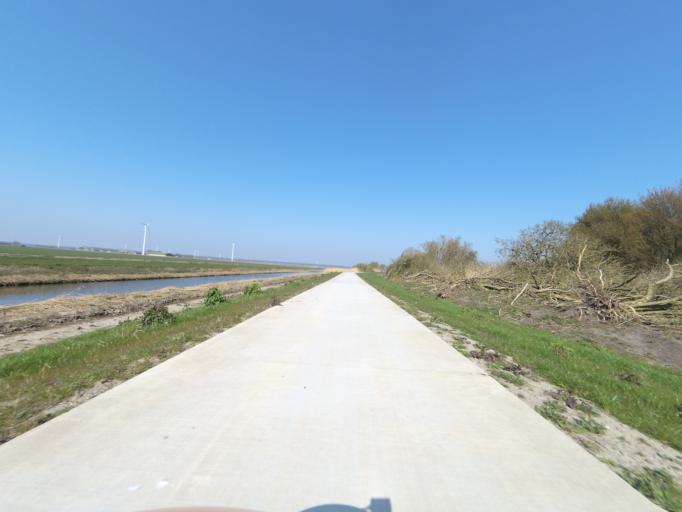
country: NL
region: Utrecht
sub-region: Gemeente Bunschoten
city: Spakenburg
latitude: 52.3498
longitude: 5.3984
